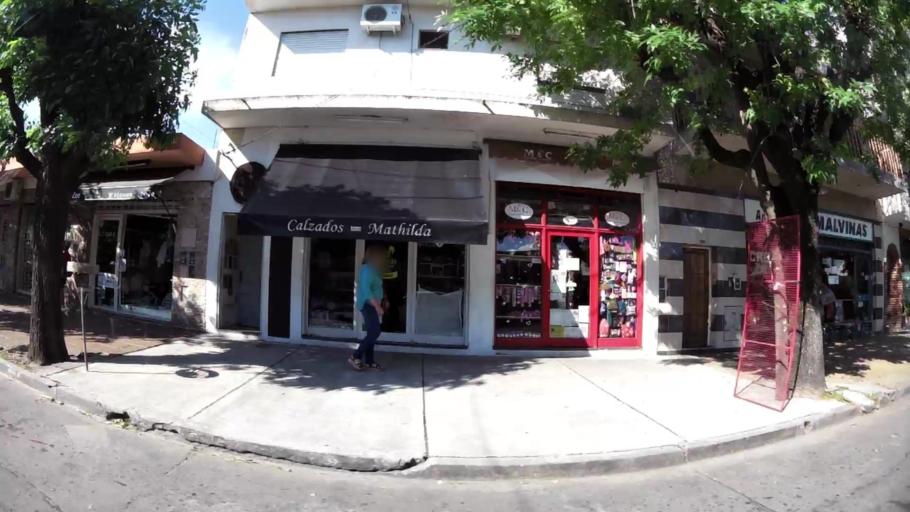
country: AR
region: Buenos Aires
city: San Justo
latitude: -34.6591
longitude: -58.5864
